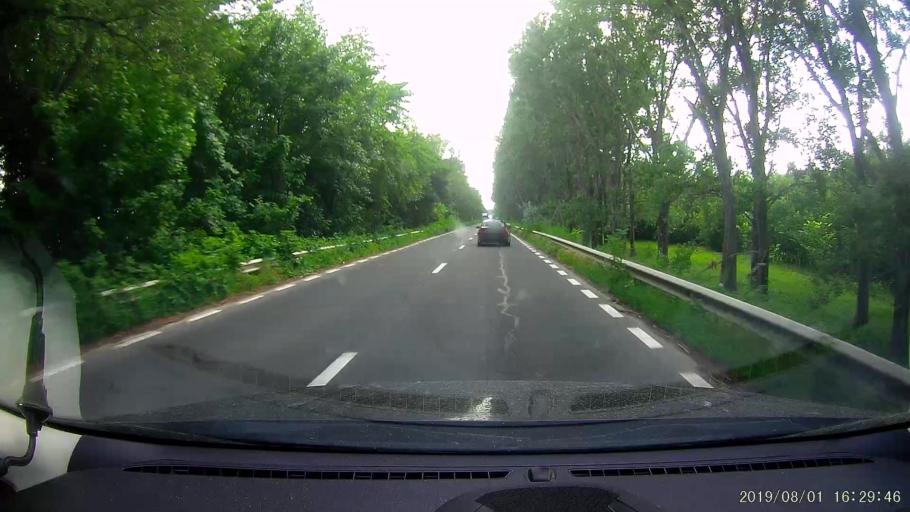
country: BG
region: Silistra
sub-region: Obshtina Silistra
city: Silistra
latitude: 44.1382
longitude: 27.2834
